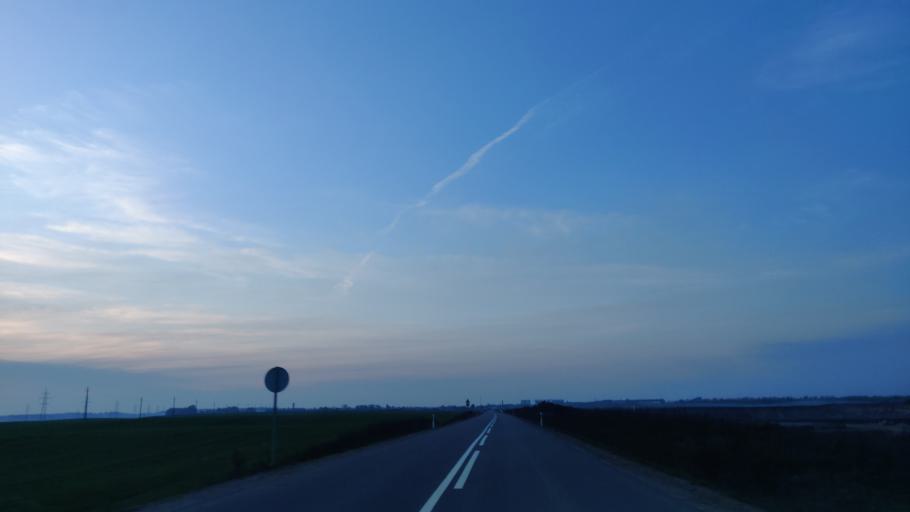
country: LT
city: Lentvaris
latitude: 54.6013
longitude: 25.0093
